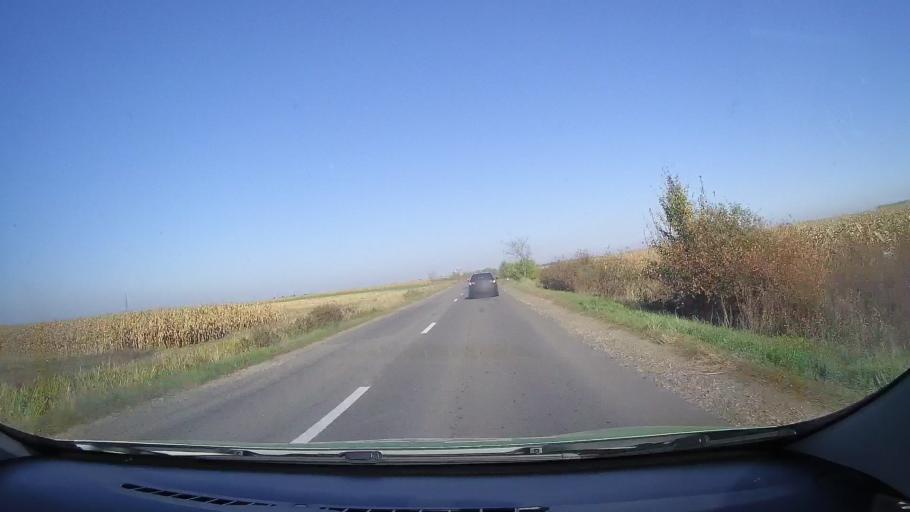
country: RO
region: Satu Mare
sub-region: Comuna Cauas
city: Cauas
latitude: 47.6135
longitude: 22.5377
